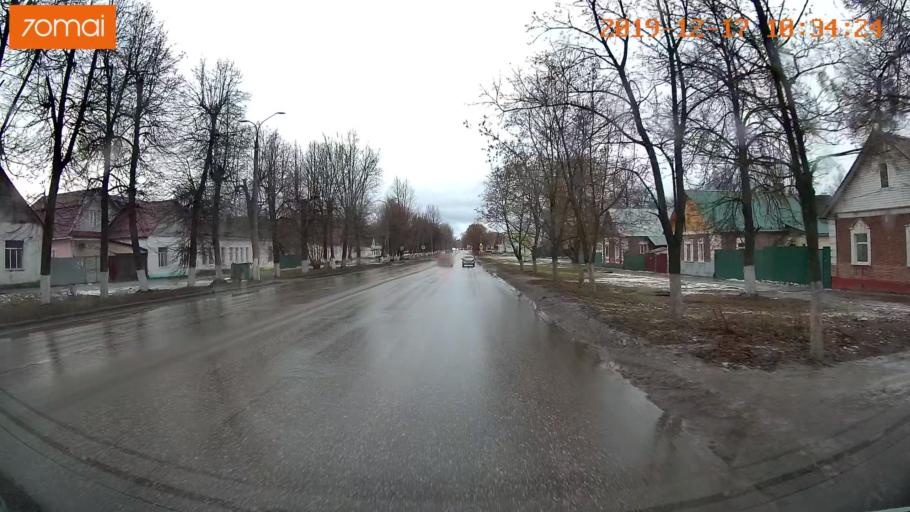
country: RU
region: Vladimir
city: Gus'-Khrustal'nyy
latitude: 55.6189
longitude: 40.6758
